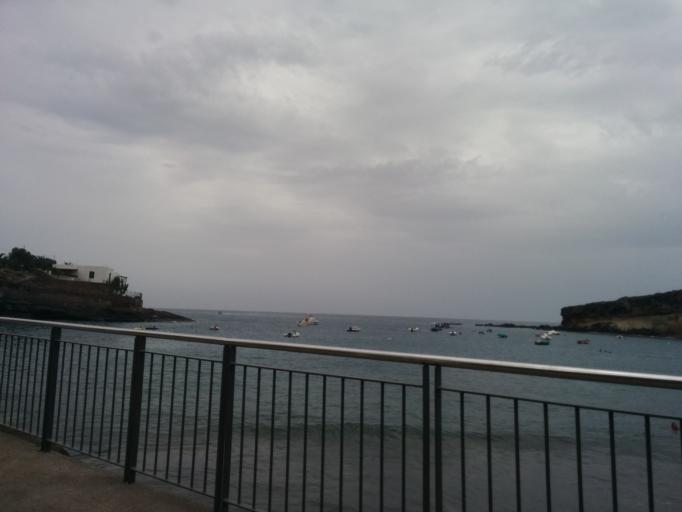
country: ES
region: Canary Islands
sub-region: Provincia de Santa Cruz de Tenerife
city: Adeje
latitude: 28.1133
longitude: -16.7679
